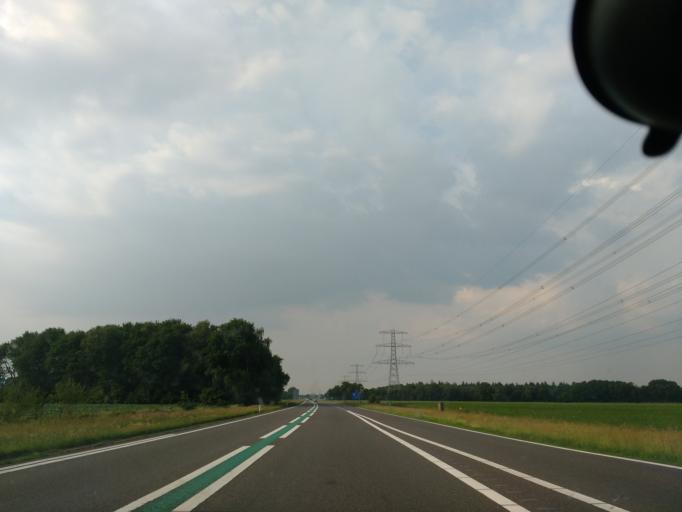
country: NL
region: Drenthe
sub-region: Gemeente Coevorden
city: Sleen
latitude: 52.7661
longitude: 6.8433
